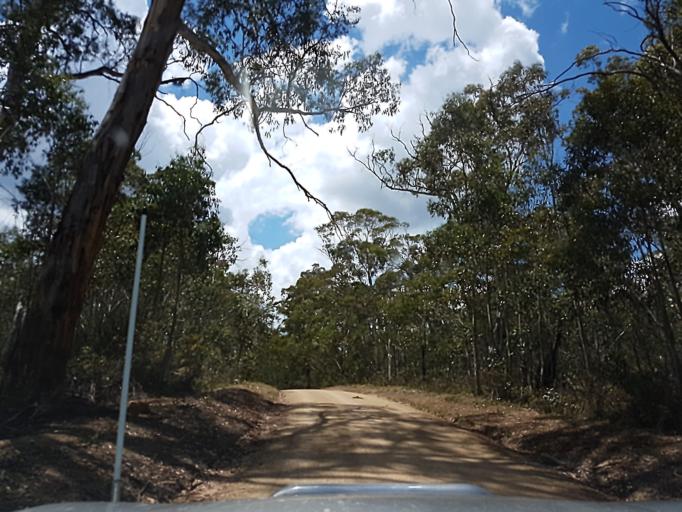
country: AU
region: New South Wales
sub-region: Snowy River
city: Jindabyne
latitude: -36.8779
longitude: 148.0793
